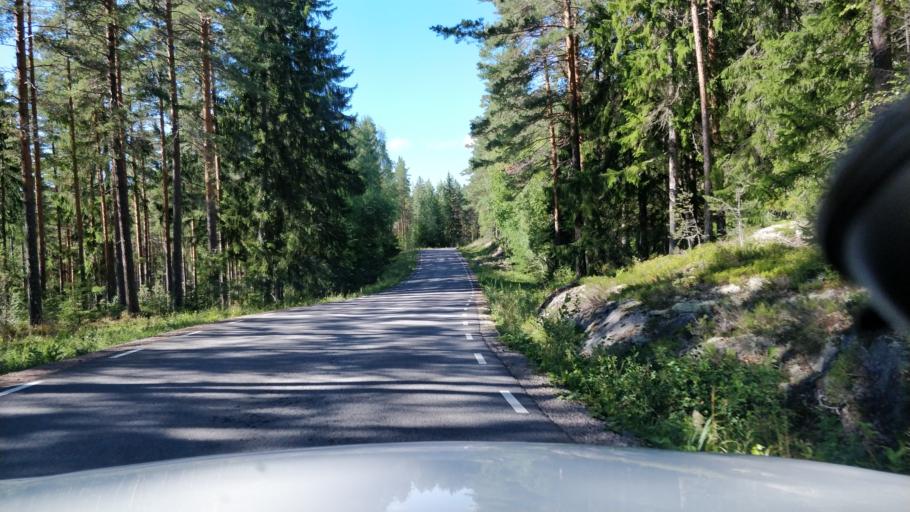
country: SE
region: Dalarna
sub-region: Faluns Kommun
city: Bjursas
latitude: 60.7455
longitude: 15.5315
